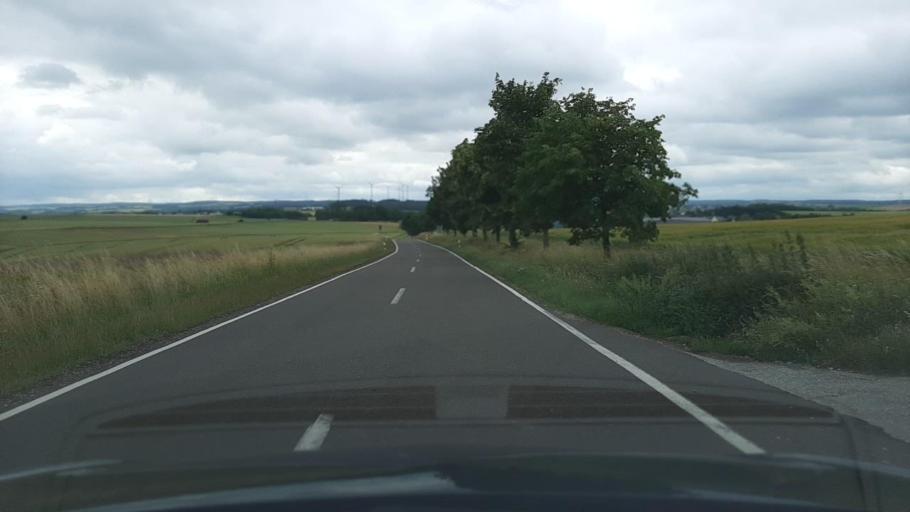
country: DE
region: Rheinland-Pfalz
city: Dommershausen
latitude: 50.1505
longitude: 7.3927
